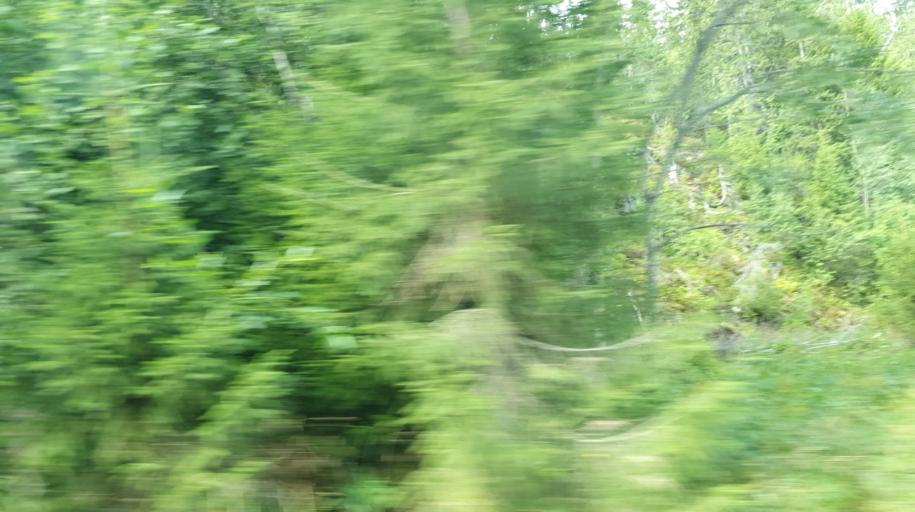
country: NO
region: Nord-Trondelag
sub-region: Levanger
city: Skogn
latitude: 63.5730
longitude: 11.2095
